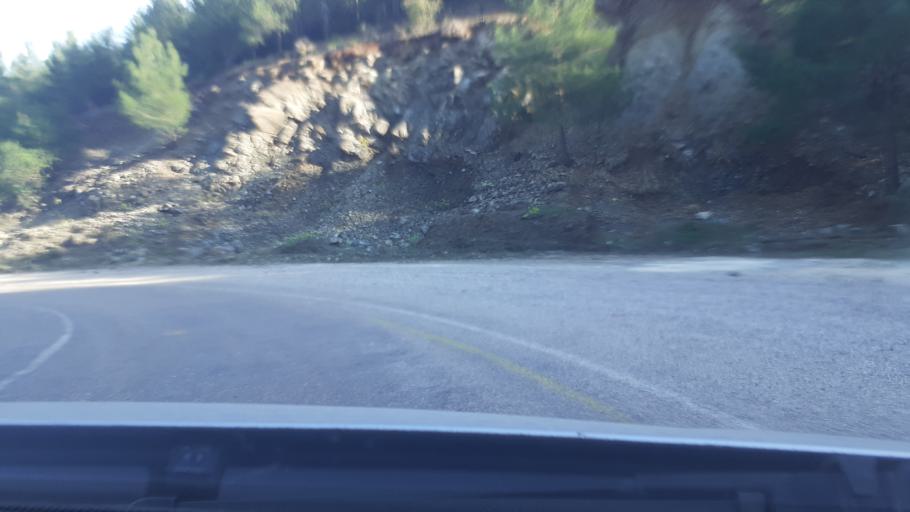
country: TR
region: Hatay
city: Aktepe
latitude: 36.7347
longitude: 36.4655
